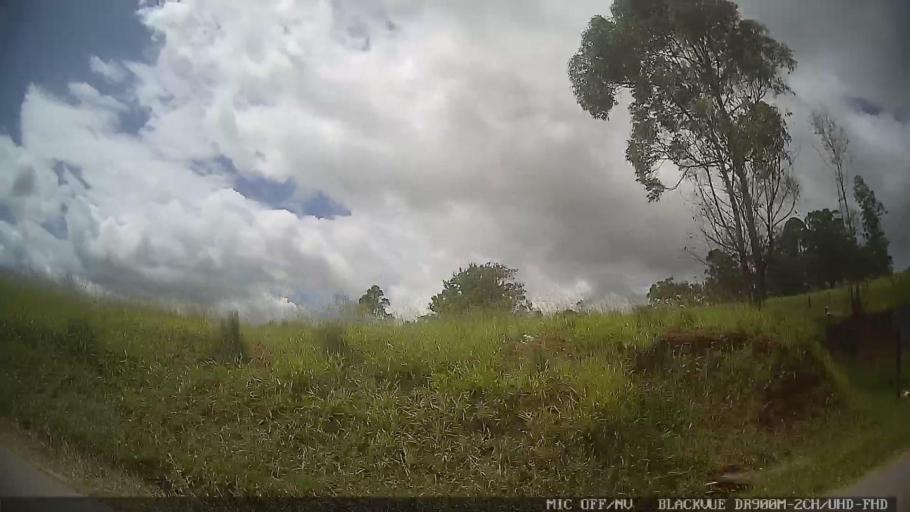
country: BR
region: Sao Paulo
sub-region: Braganca Paulista
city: Braganca Paulista
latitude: -22.8157
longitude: -46.5433
